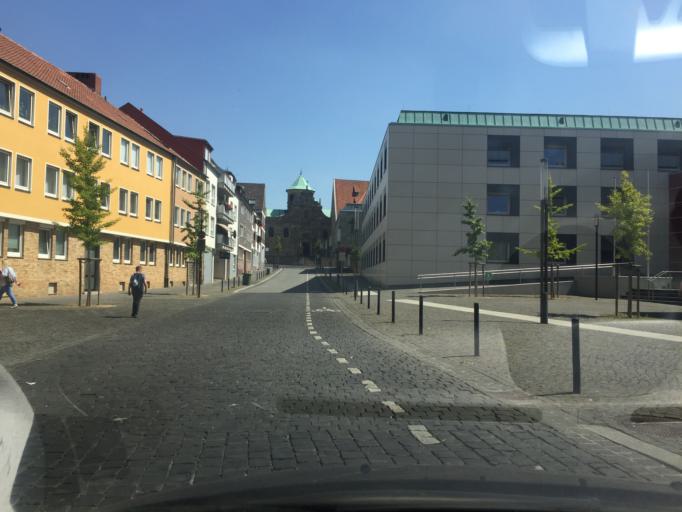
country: DE
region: Lower Saxony
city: Hildesheim
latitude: 52.1496
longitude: 9.9484
